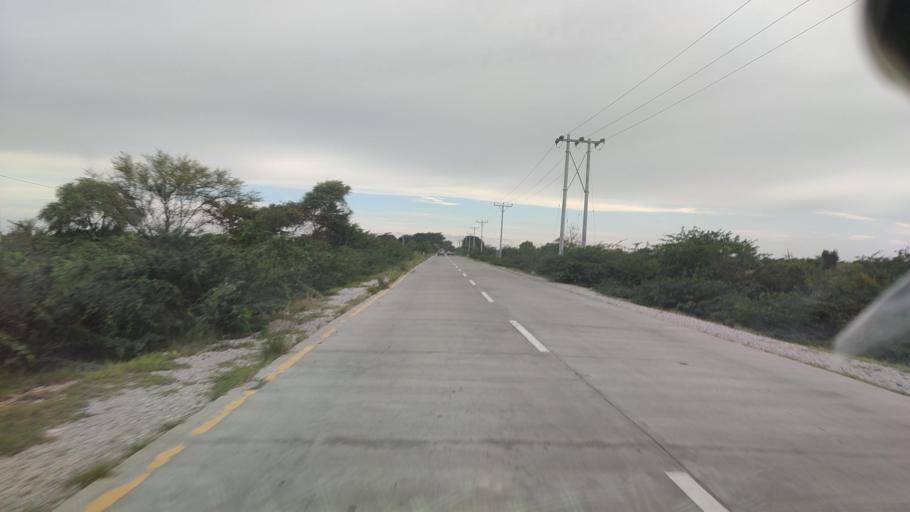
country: MM
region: Mandalay
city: Kyaukse
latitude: 21.3175
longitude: 96.0222
